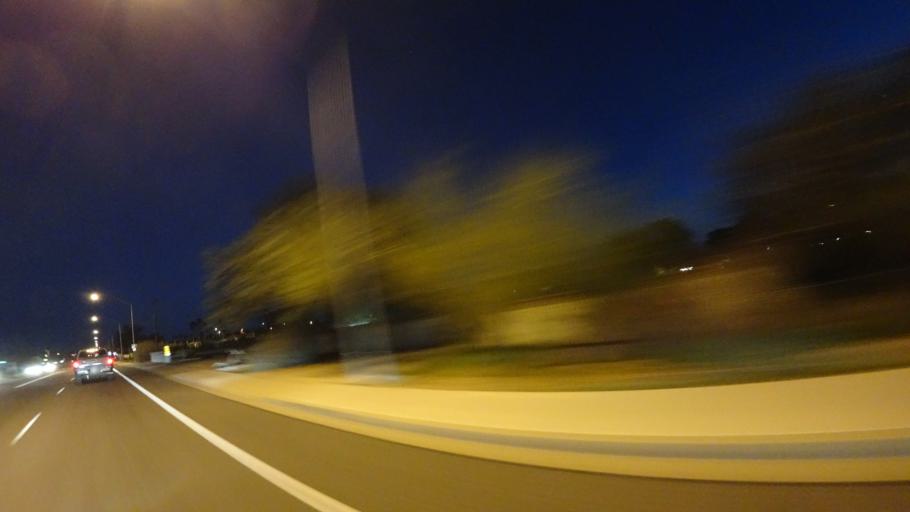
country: US
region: Arizona
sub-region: Maricopa County
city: Mesa
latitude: 33.4517
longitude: -111.7795
